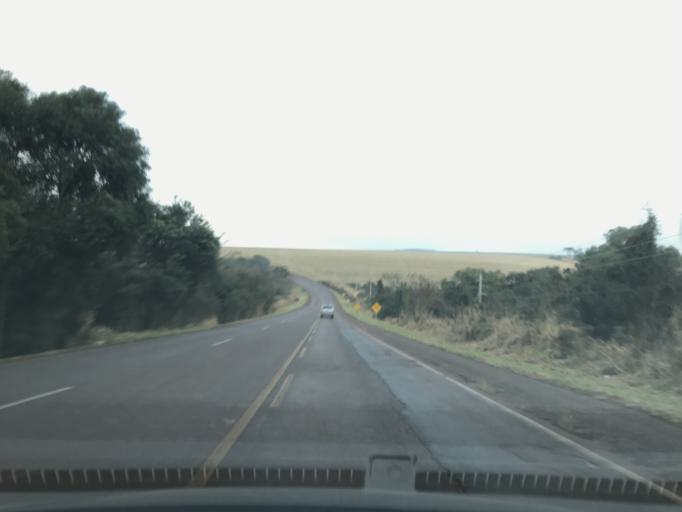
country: BR
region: Parana
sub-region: Toledo
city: Toledo
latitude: -24.6353
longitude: -53.7116
